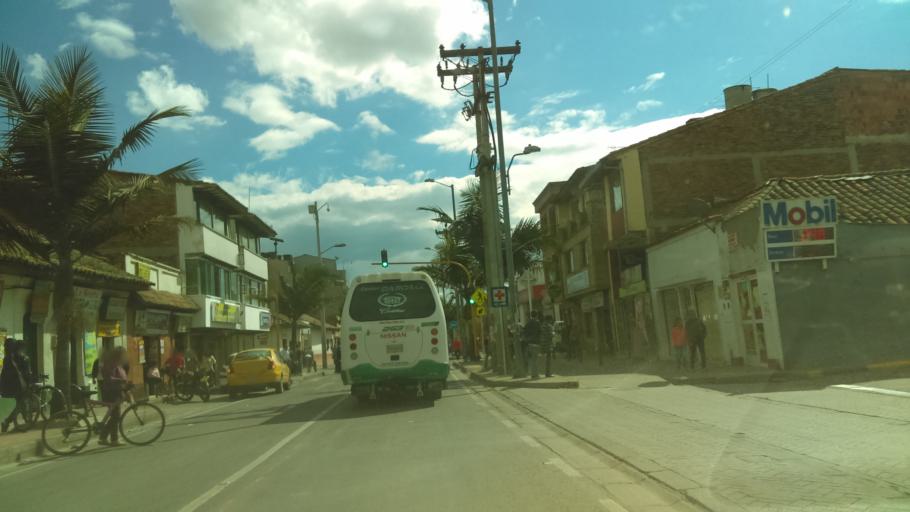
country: CO
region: Cundinamarca
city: Cajica
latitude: 4.9176
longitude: -74.0264
